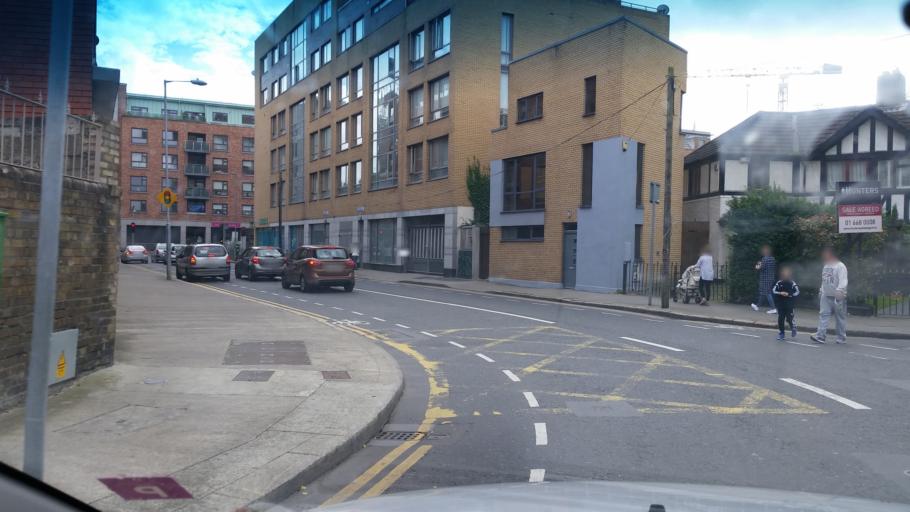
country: IE
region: Leinster
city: Rialto
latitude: 53.3379
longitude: -6.2872
